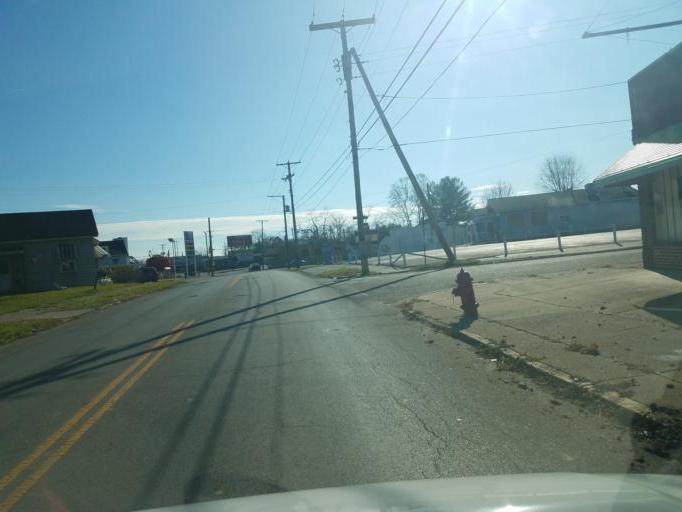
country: US
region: Ohio
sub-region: Scioto County
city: Sciotodale
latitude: 38.7614
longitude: -82.8933
